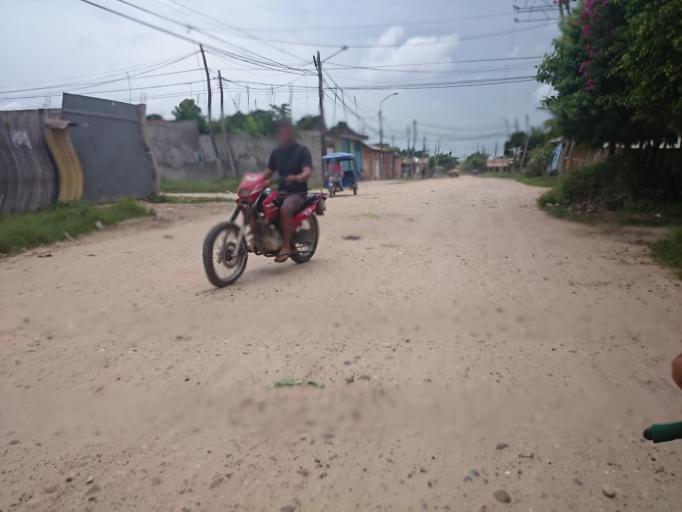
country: PE
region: Ucayali
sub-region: Provincia de Coronel Portillo
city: Pucallpa
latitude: -8.3753
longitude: -74.5557
